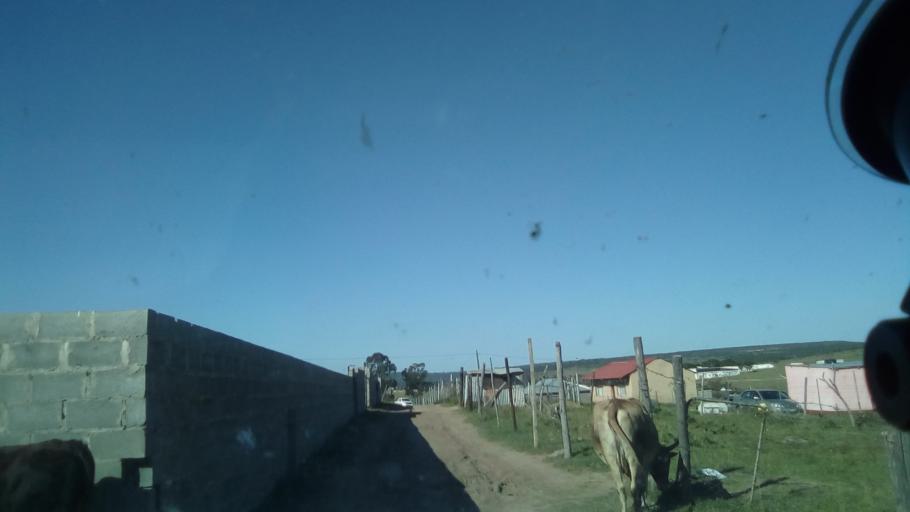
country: ZA
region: Eastern Cape
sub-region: Buffalo City Metropolitan Municipality
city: Bhisho
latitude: -32.8284
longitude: 27.3706
